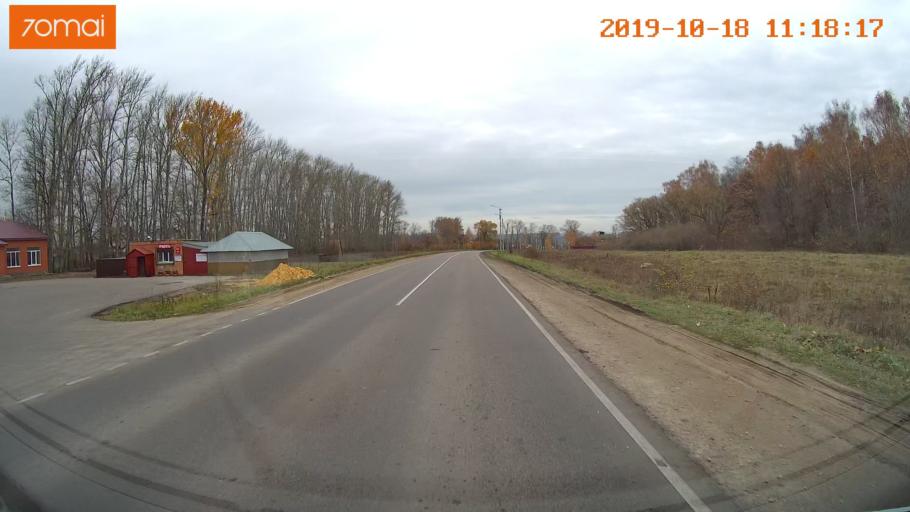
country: RU
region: Tula
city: Kimovsk
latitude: 54.0373
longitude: 38.5503
